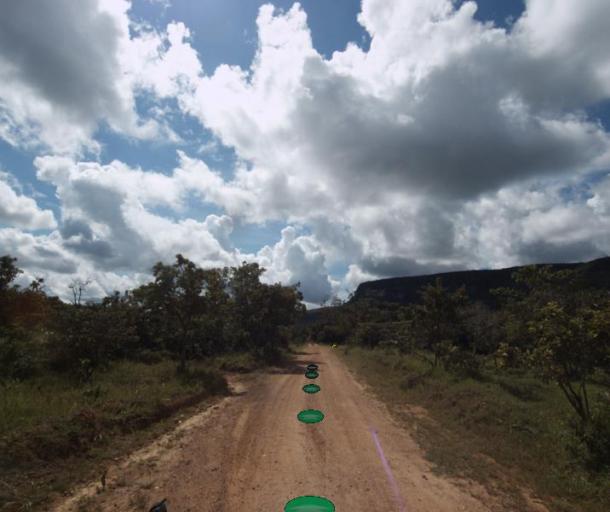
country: BR
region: Goias
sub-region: Pirenopolis
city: Pirenopolis
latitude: -15.7806
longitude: -48.9366
